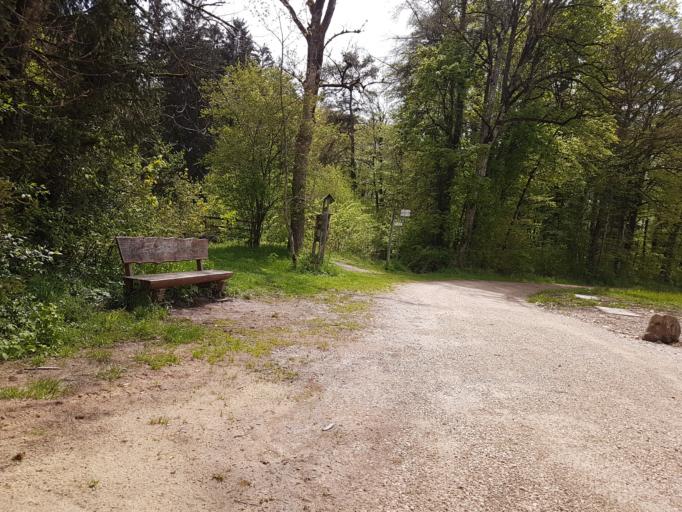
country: CH
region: Schaffhausen
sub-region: Bezirk Schleitheim
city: Schleitheim
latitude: 47.7665
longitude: 8.4774
